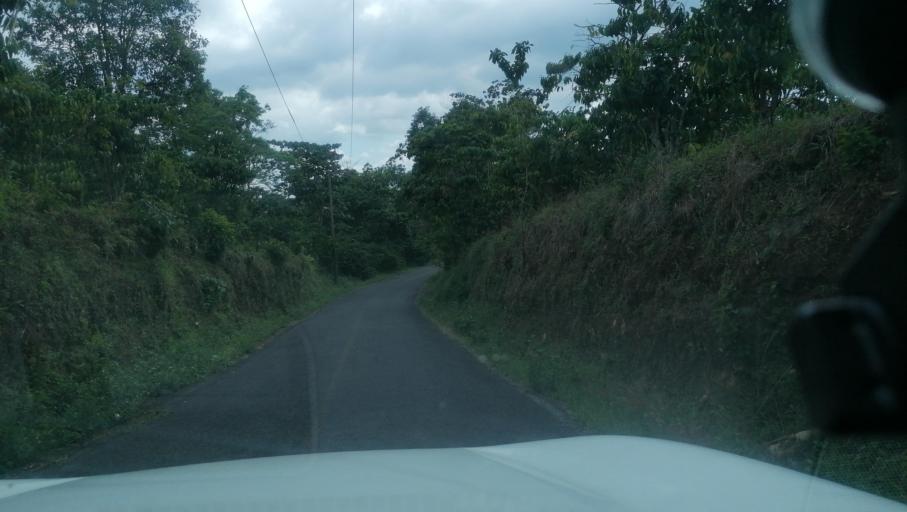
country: MX
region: Chiapas
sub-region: Cacahoatan
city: Benito Juarez
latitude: 15.0585
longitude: -92.1513
